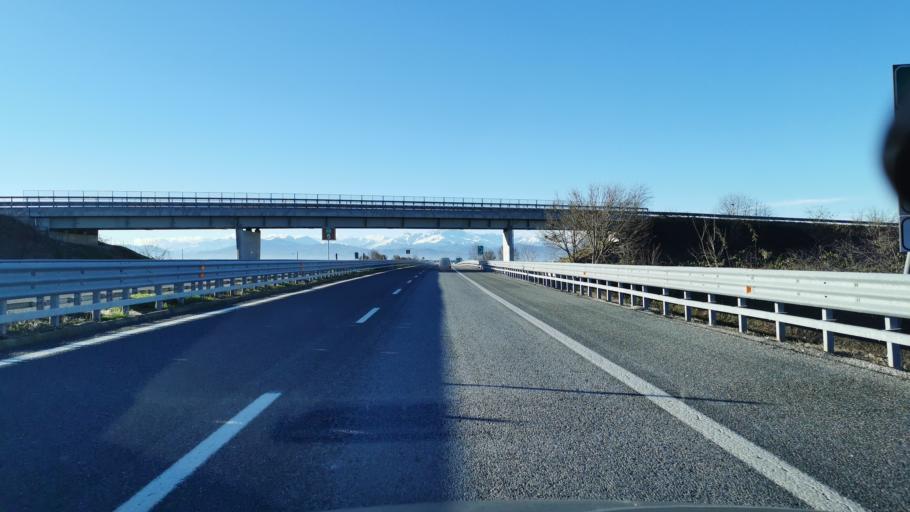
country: IT
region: Piedmont
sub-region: Provincia di Cuneo
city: Sant'Albano Stura
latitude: 44.4704
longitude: 7.7124
